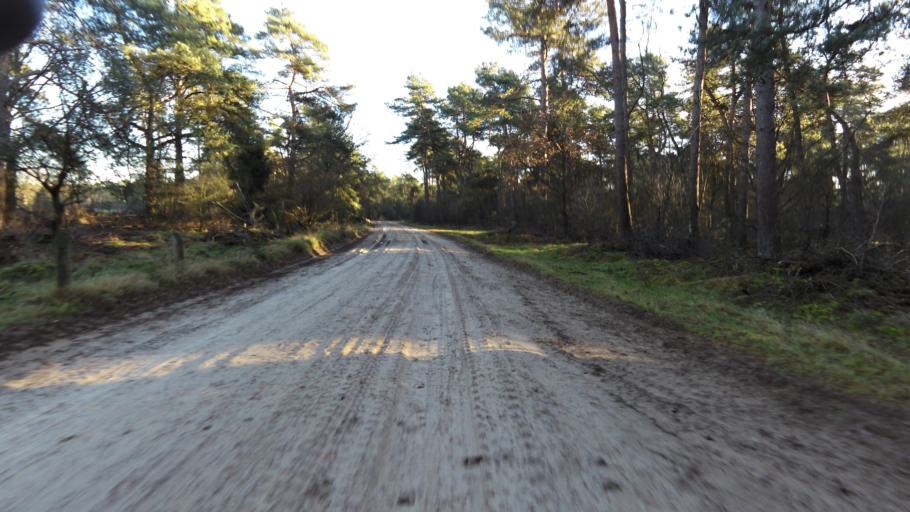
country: NL
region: Gelderland
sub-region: Gemeente Barneveld
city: Garderen
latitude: 52.2071
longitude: 5.7317
